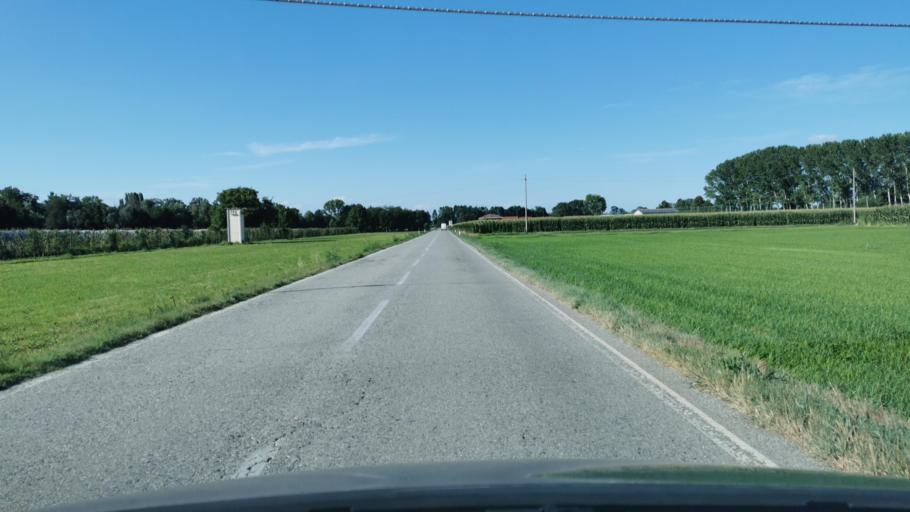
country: IT
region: Piedmont
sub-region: Provincia di Cuneo
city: Genola
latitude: 44.6043
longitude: 7.6226
